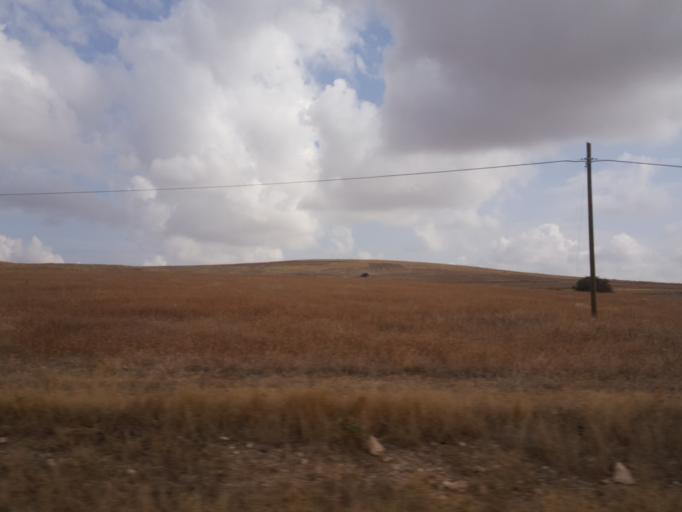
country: TR
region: Kirikkale
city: Keskin
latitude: 39.6364
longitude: 33.6080
